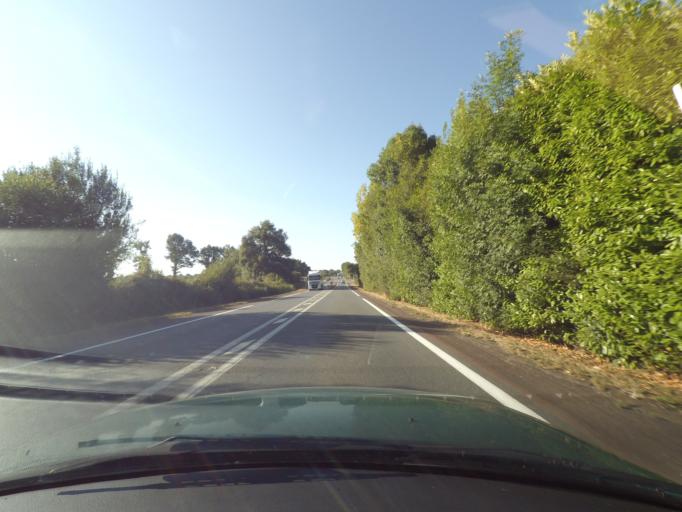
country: FR
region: Poitou-Charentes
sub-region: Departement des Deux-Sevres
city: Chiche
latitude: 46.7472
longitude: -0.3059
